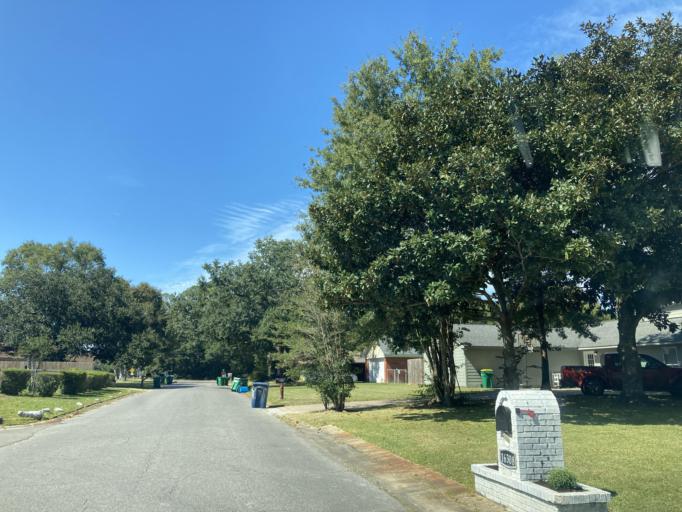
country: US
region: Mississippi
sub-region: Jackson County
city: Saint Martin
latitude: 30.4505
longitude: -88.8820
